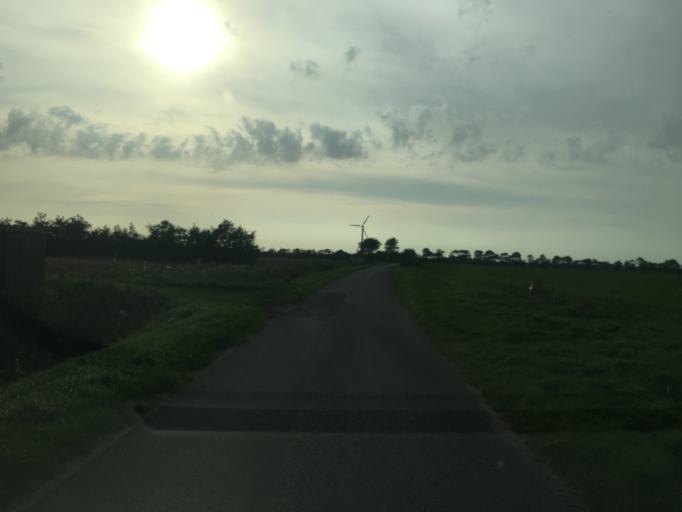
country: DE
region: Schleswig-Holstein
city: Bramstedtlund
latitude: 54.9129
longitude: 9.0528
